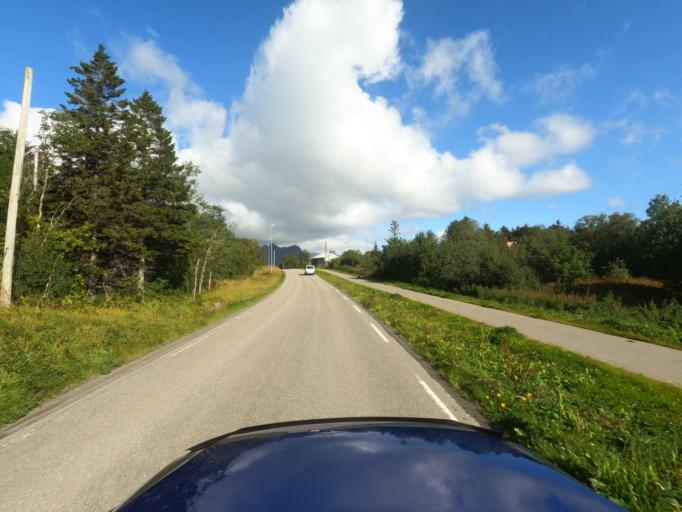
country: NO
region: Nordland
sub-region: Vestvagoy
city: Evjen
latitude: 68.1479
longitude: 13.8421
